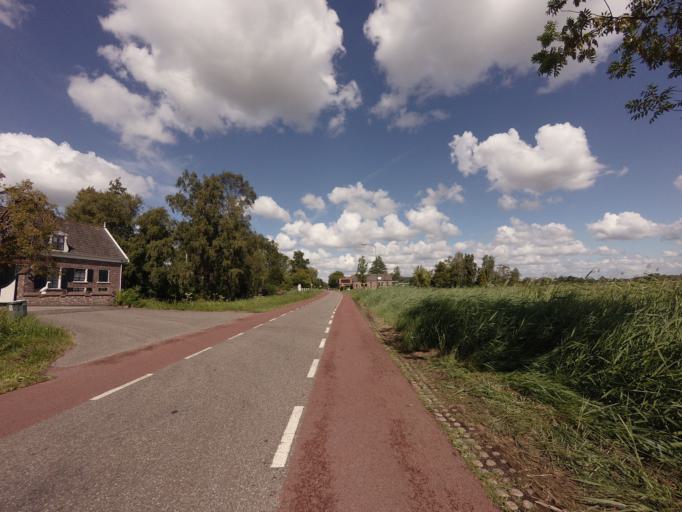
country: NL
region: Utrecht
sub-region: Stichtse Vecht
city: Breukelen
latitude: 52.1703
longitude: 4.9475
